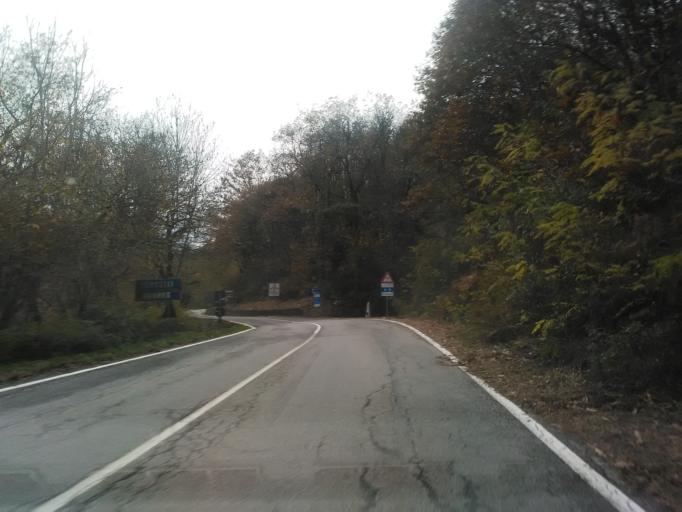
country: IT
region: Piedmont
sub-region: Provincia di Novara
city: Pogno
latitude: 45.7439
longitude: 8.3696
